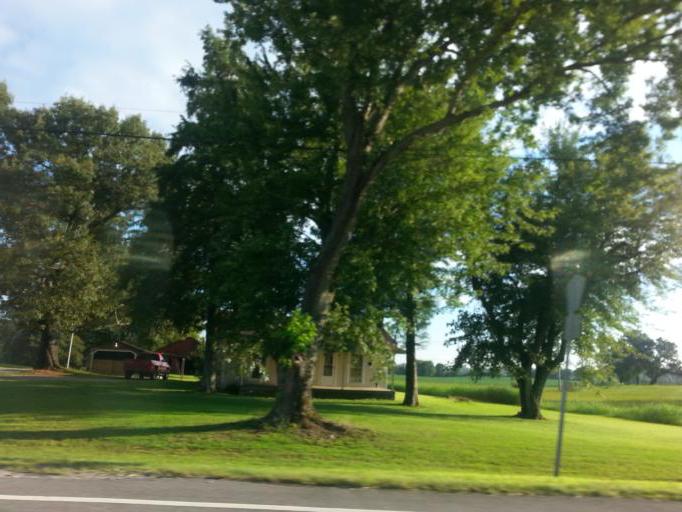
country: US
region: Alabama
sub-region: Lauderdale County
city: Rogersville
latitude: 34.8465
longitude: -87.3823
